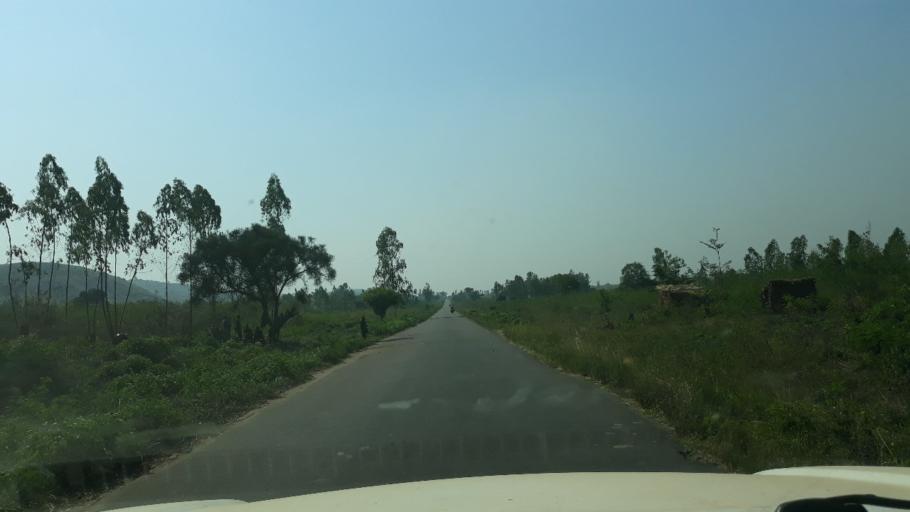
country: CD
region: South Kivu
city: Uvira
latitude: -3.2189
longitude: 29.1651
